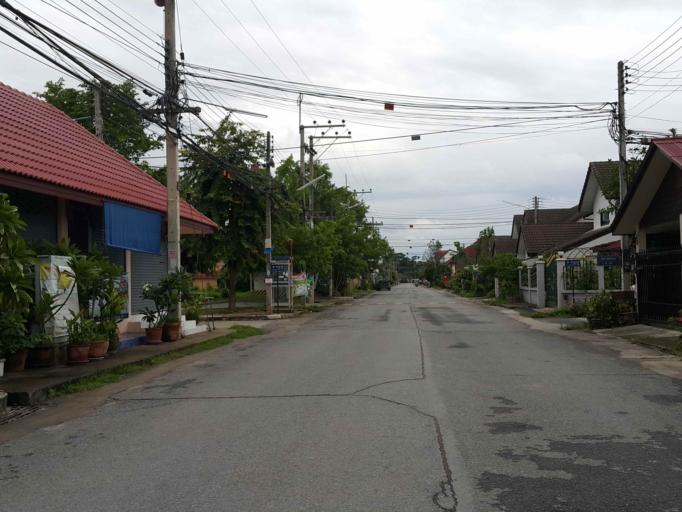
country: TH
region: Chiang Mai
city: San Sai
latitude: 18.8278
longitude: 99.0553
